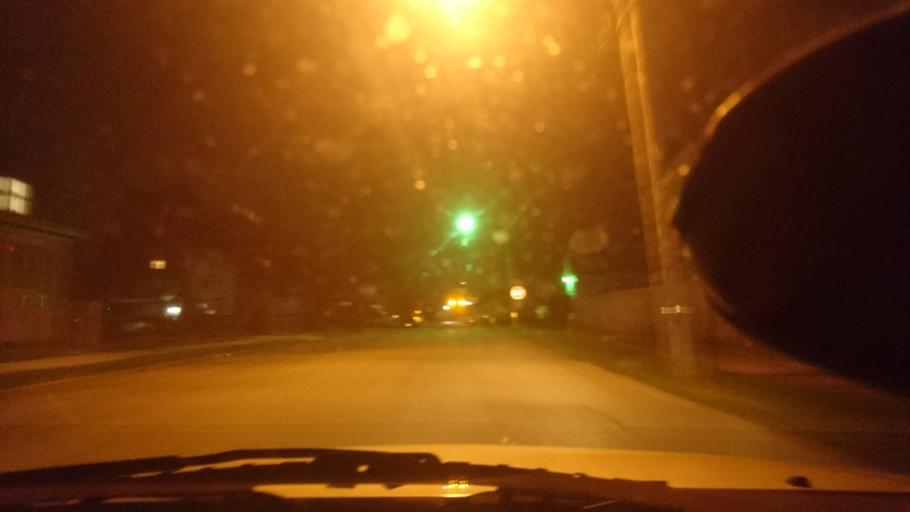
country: US
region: Pennsylvania
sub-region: Delaware County
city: Chester
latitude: 39.8661
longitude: -75.3602
